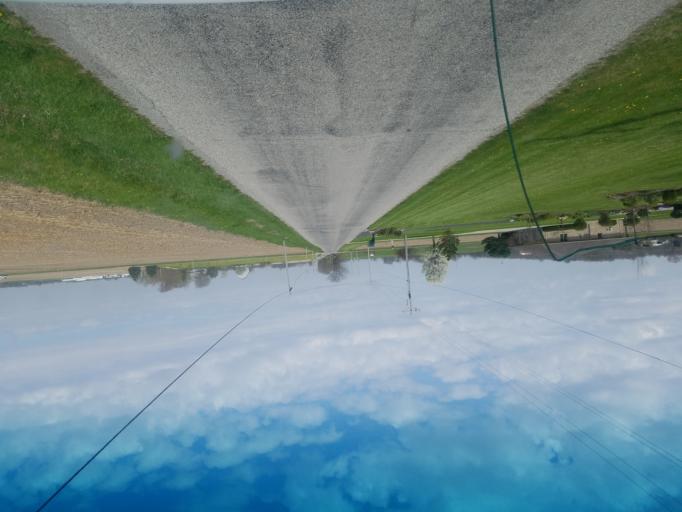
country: US
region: Ohio
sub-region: Logan County
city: Northwood
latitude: 40.4904
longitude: -83.7383
